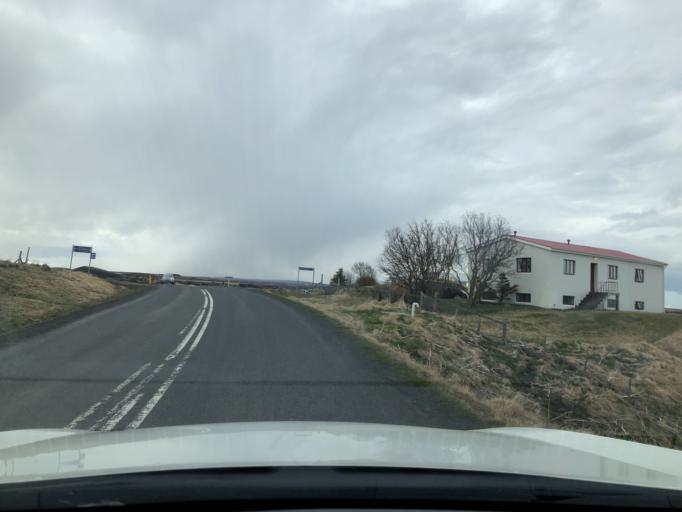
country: IS
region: Northeast
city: Laugar
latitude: 65.5692
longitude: -17.0452
